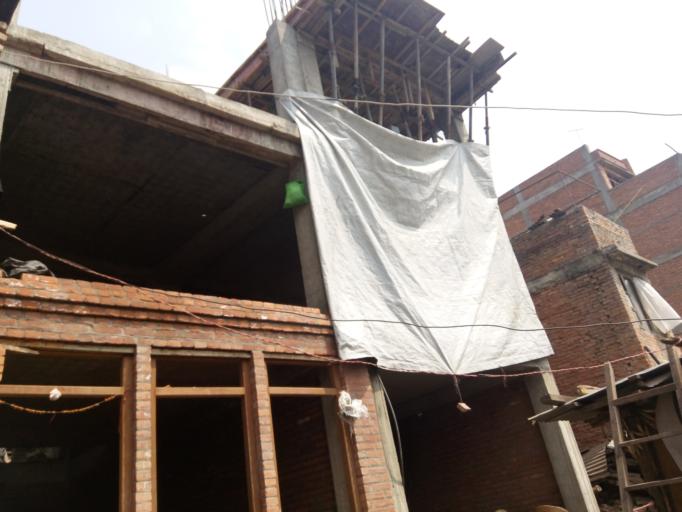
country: NP
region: Central Region
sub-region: Bagmati Zone
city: Bhaktapur
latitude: 27.6701
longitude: 85.4321
